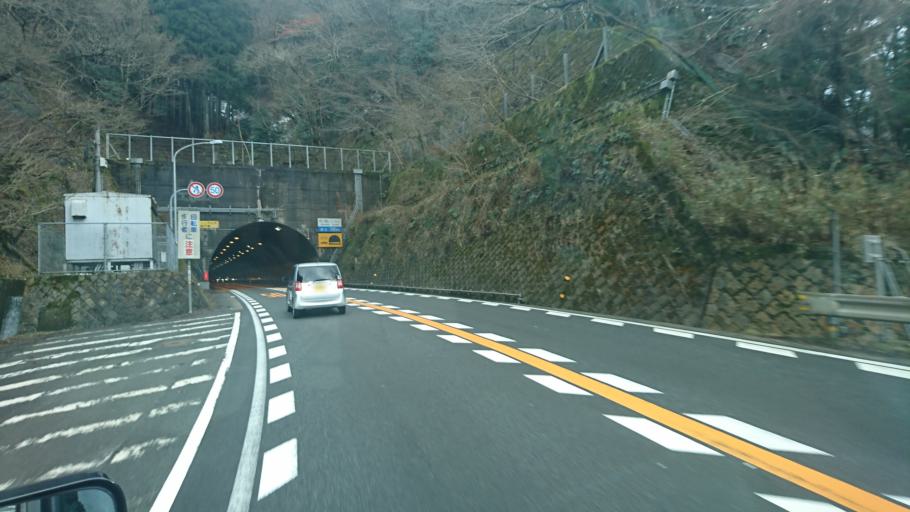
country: JP
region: Hyogo
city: Toyooka
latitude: 35.4858
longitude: 134.5760
